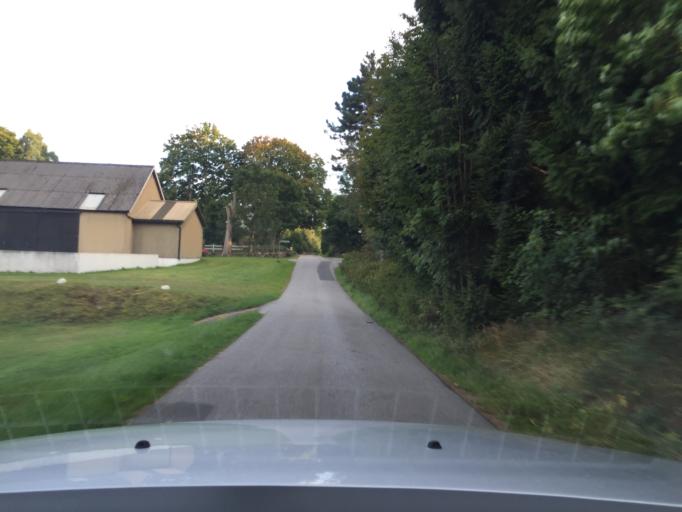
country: SE
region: Skane
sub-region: Hassleholms Kommun
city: Sosdala
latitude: 55.9899
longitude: 13.6043
